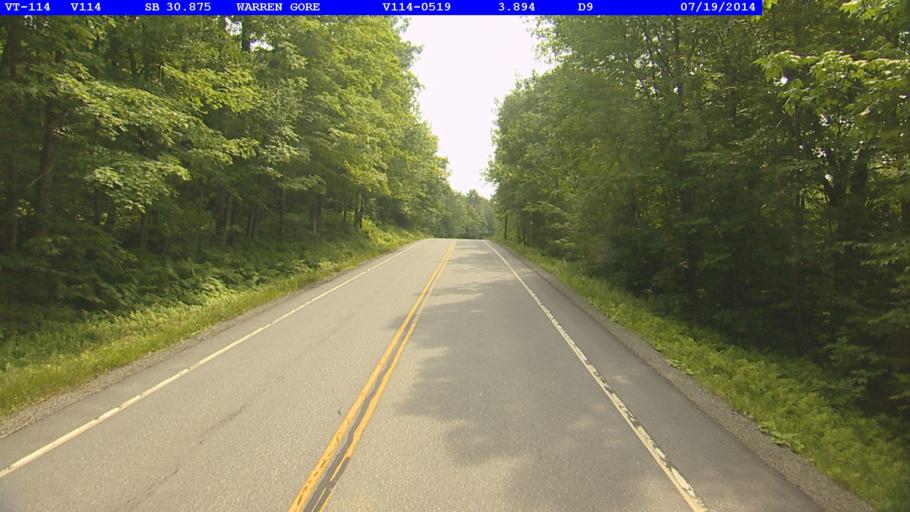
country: CA
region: Quebec
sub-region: Estrie
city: Coaticook
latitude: 44.9358
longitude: -71.8588
